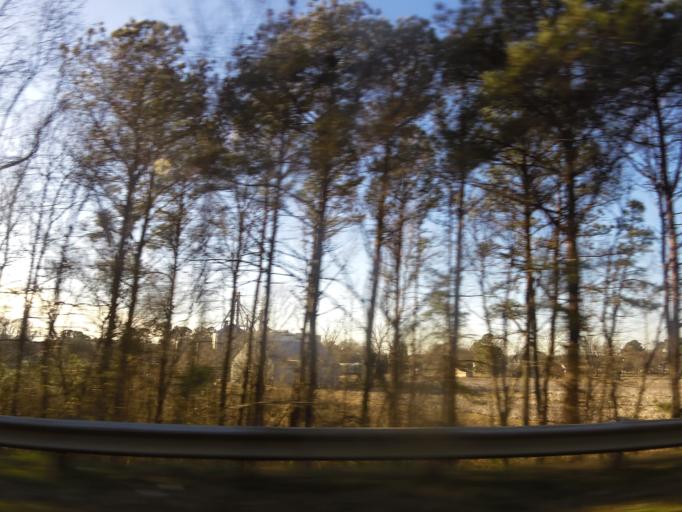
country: US
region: Virginia
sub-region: Isle of Wight County
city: Windsor
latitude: 36.6819
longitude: -76.7727
